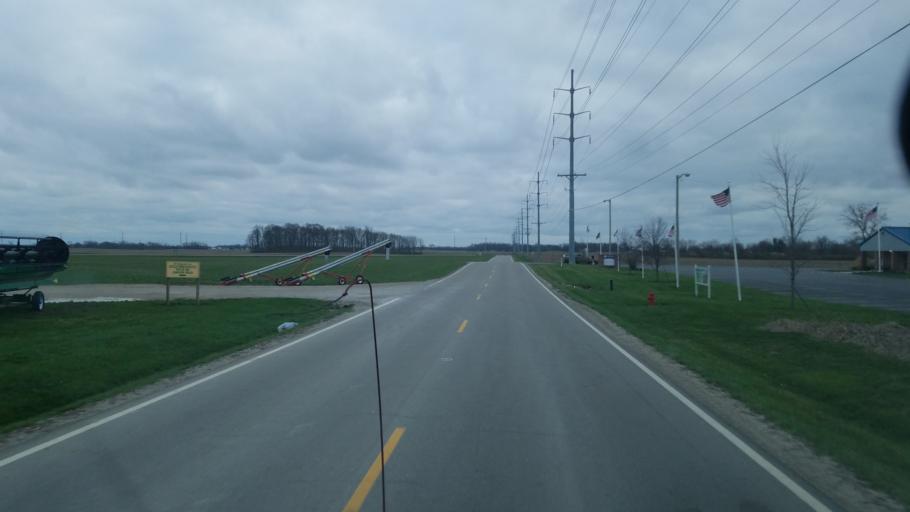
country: US
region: Ohio
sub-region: Fayette County
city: Washington Court House
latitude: 39.5216
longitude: -83.4711
